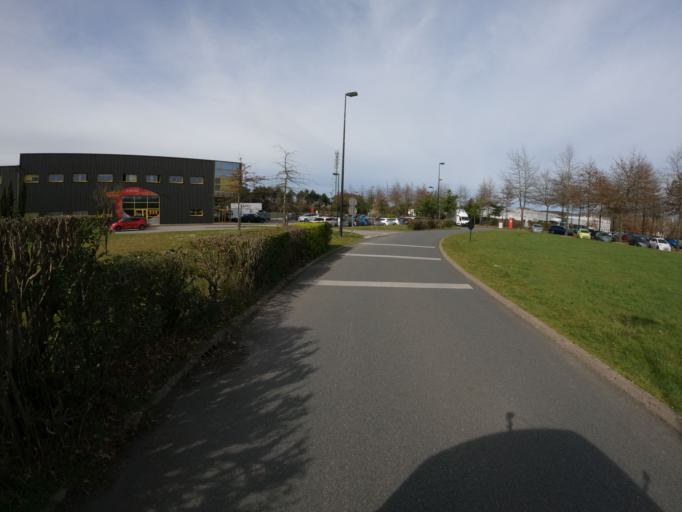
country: FR
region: Pays de la Loire
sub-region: Departement de la Vendee
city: Bouffere
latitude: 46.9558
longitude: -1.3532
